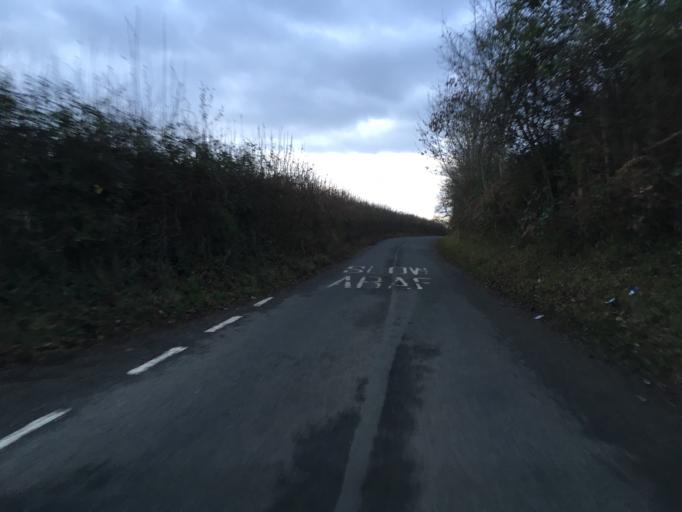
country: GB
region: Wales
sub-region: Newport
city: Bishton
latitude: 51.5963
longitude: -2.8812
